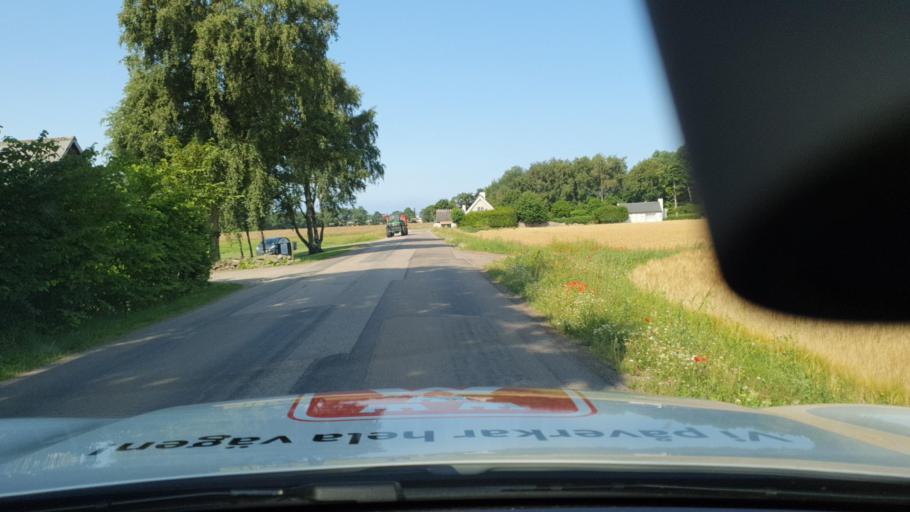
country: SE
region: Skane
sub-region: Hoganas Kommun
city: Hoganas
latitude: 56.2115
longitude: 12.5712
